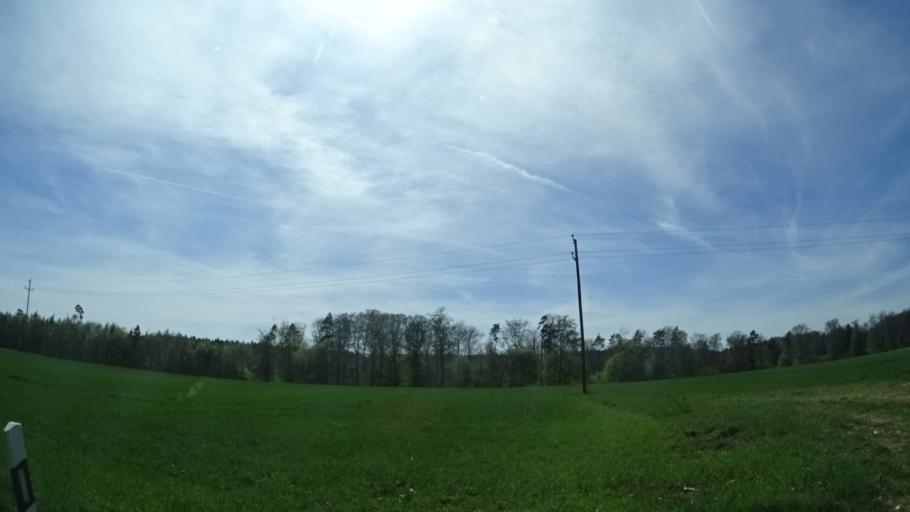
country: DE
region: Bavaria
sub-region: Regierungsbezirk Unterfranken
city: Maroldsweisach
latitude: 50.1770
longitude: 10.6272
